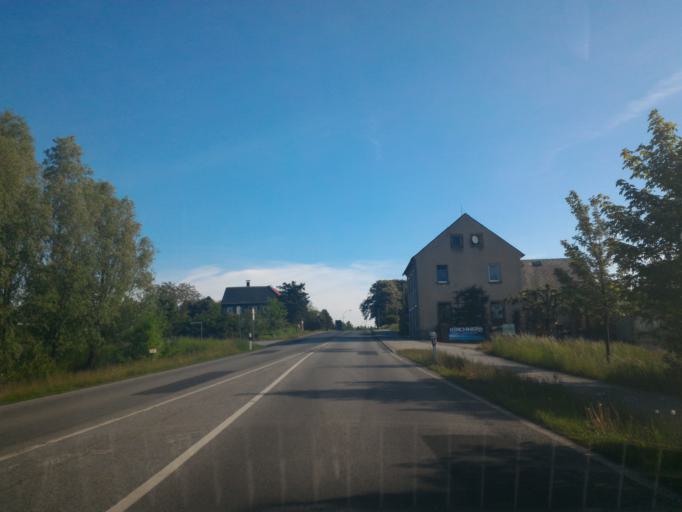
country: DE
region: Saxony
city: Lobau
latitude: 51.0810
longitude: 14.6574
